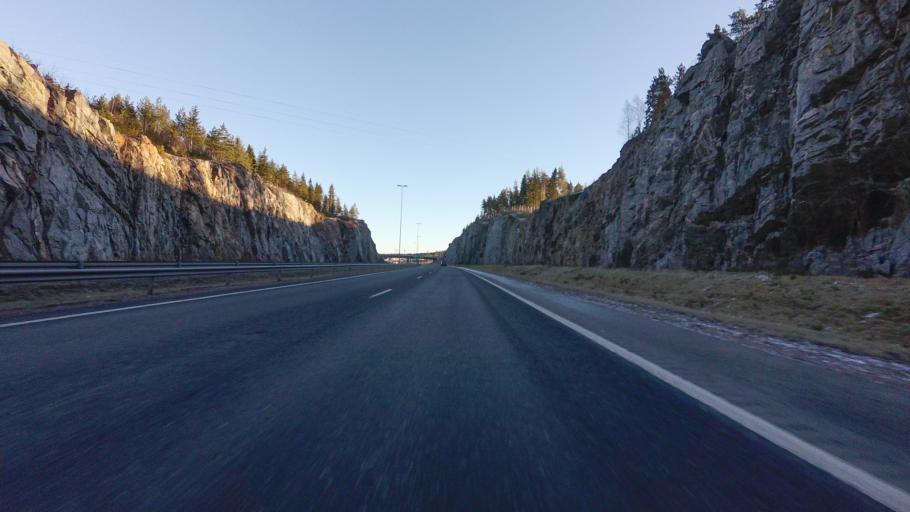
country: FI
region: Uusimaa
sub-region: Helsinki
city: Lohja
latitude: 60.2831
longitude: 24.1002
